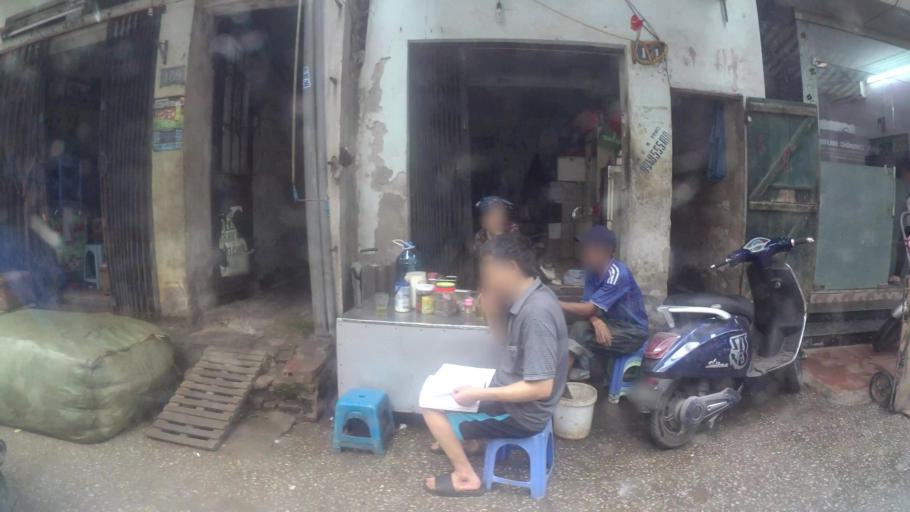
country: VN
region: Ha Noi
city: Hoan Kiem
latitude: 21.0377
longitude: 105.8553
